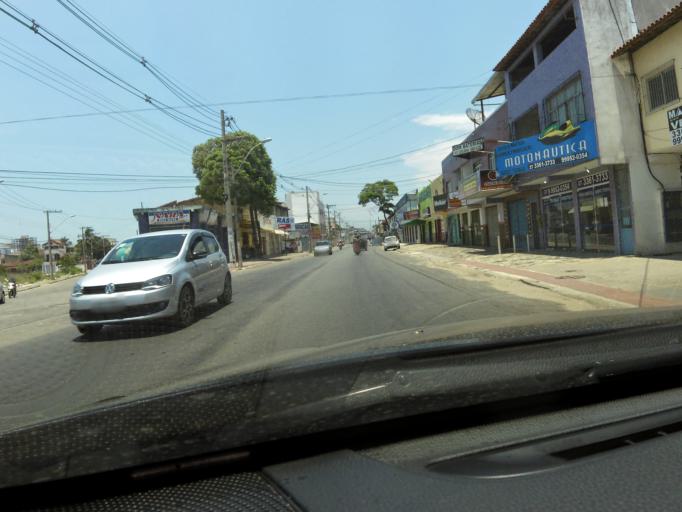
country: BR
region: Espirito Santo
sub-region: Guarapari
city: Guarapari
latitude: -20.6514
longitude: -40.4946
